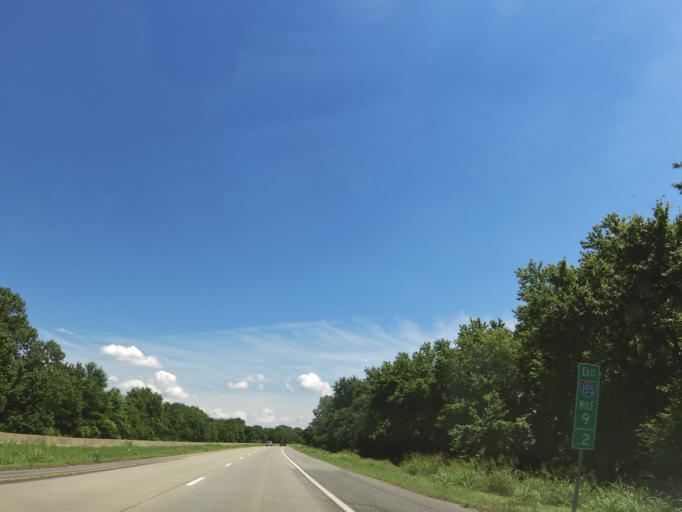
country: US
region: Missouri
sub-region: Pemiscot County
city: Caruthersville
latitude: 36.1318
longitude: -89.6246
